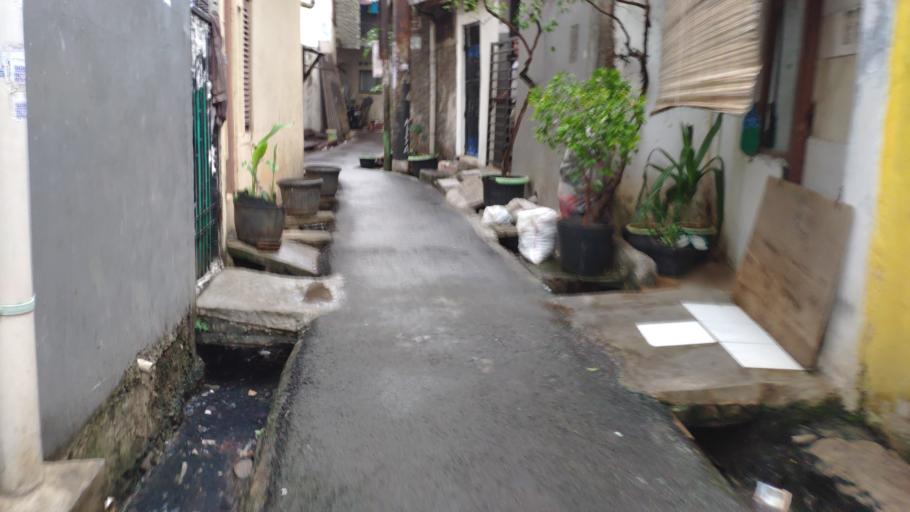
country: ID
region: Jakarta Raya
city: Jakarta
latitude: -6.2066
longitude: 106.8699
